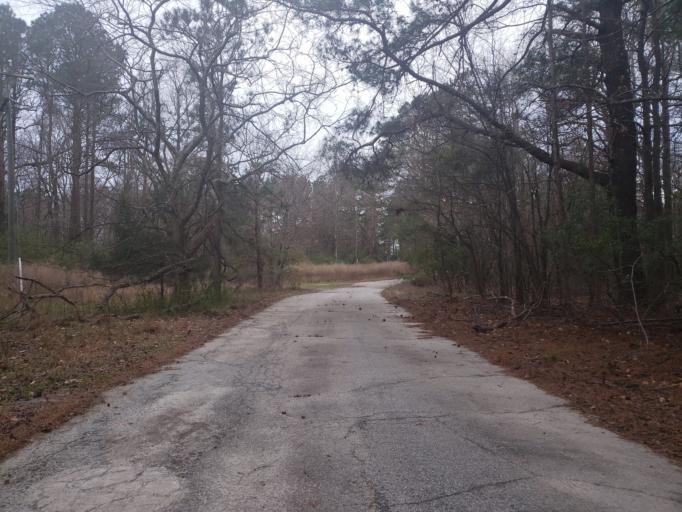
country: US
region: Virginia
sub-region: City of Newport News
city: Newport News
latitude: 36.8972
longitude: -76.4314
